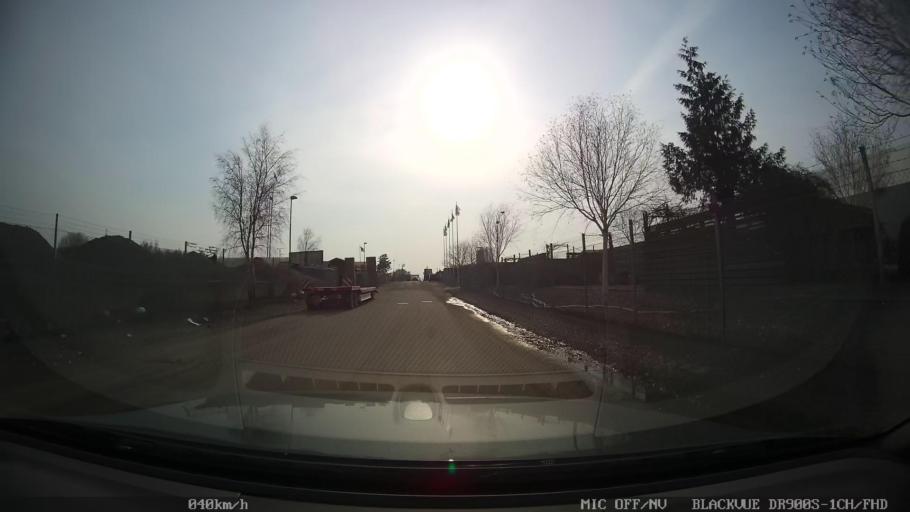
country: SE
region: Skane
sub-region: Ystads Kommun
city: Ystad
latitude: 55.4444
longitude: 13.8534
